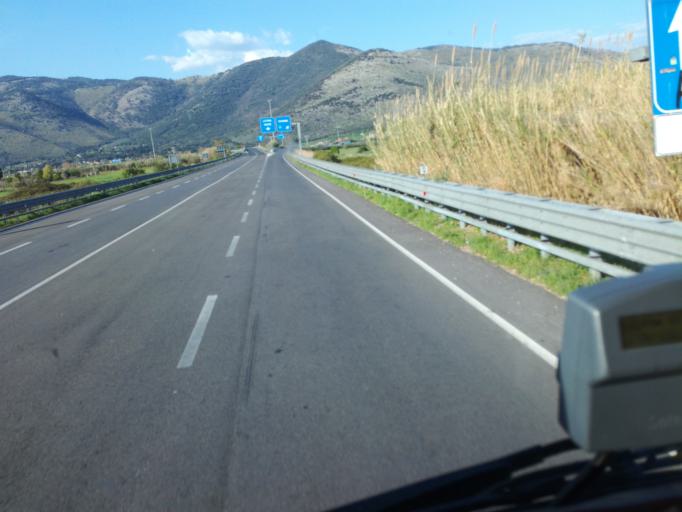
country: IT
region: Latium
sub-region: Provincia di Latina
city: Roccasecca dei Volsci
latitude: 41.4896
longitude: 13.2068
